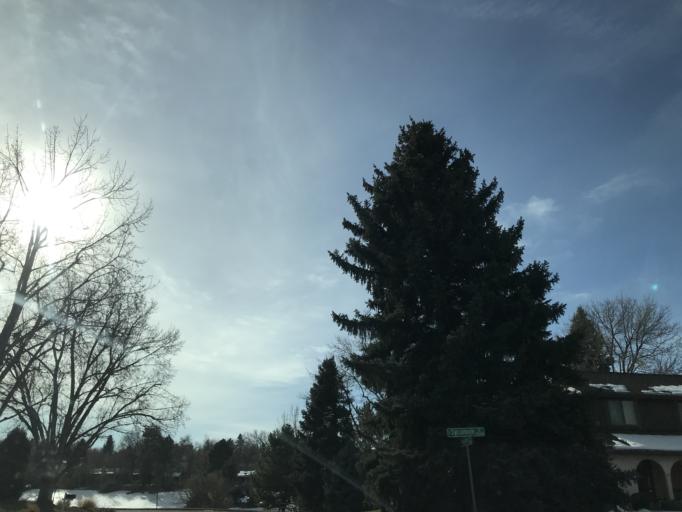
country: US
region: Colorado
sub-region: Arapahoe County
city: Littleton
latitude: 39.5969
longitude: -105.0148
